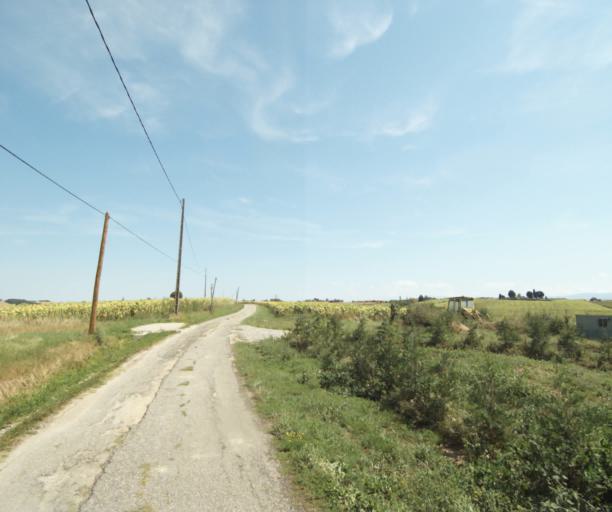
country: FR
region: Midi-Pyrenees
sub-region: Departement de l'Ariege
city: Lezat-sur-Leze
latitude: 43.2467
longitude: 1.3863
